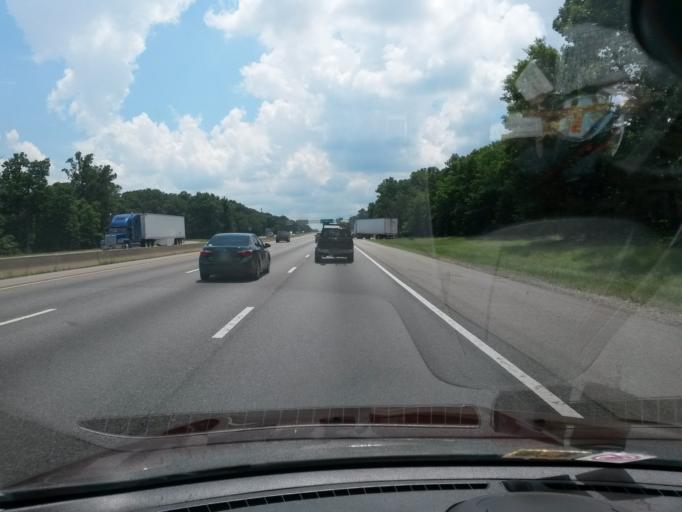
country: US
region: Virginia
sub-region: Chesterfield County
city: Chester
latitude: 37.3582
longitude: -77.4044
